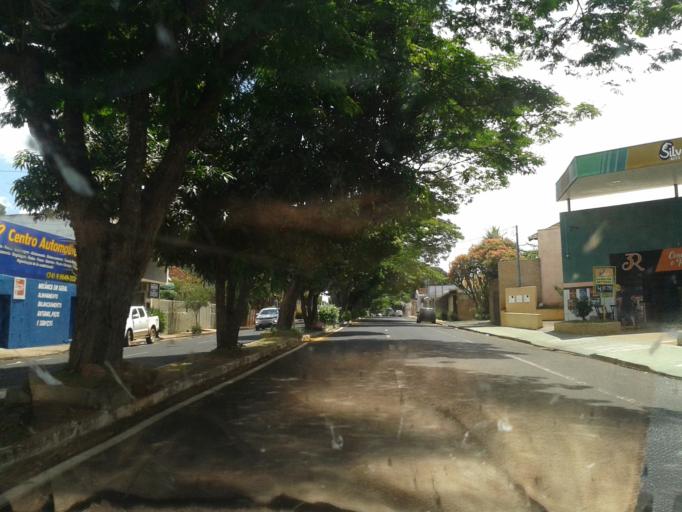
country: BR
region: Minas Gerais
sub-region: Uberaba
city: Uberaba
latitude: -19.7440
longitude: -47.9494
